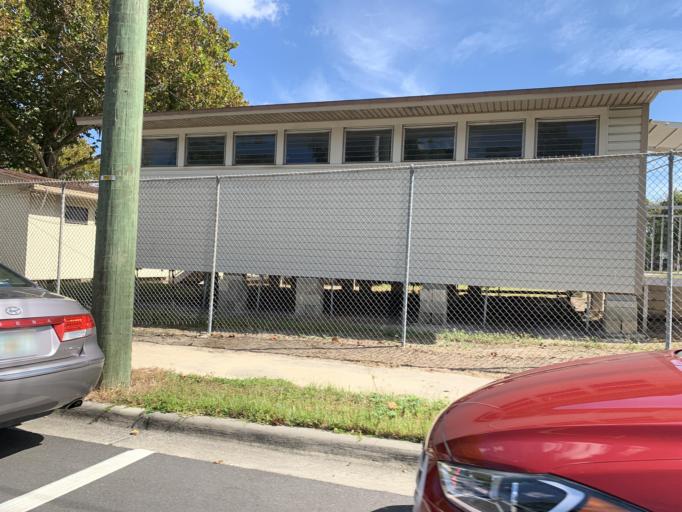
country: US
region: Florida
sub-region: Marion County
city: Ocala
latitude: 29.1816
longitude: -82.1342
